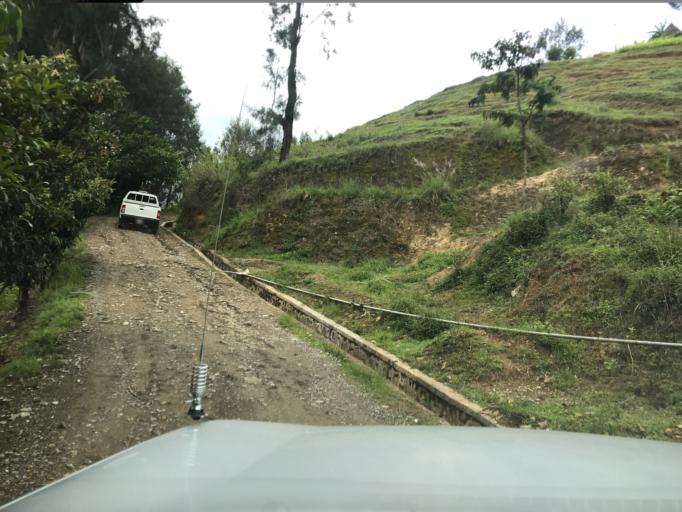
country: TL
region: Aileu
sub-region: Aileu Villa
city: Aileu
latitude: -8.8514
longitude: 125.5861
